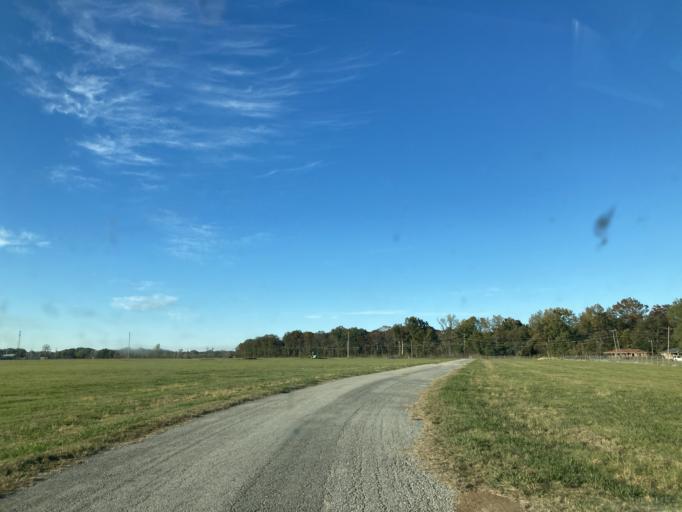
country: US
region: Mississippi
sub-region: Yazoo County
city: Yazoo City
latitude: 32.8803
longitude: -90.4202
